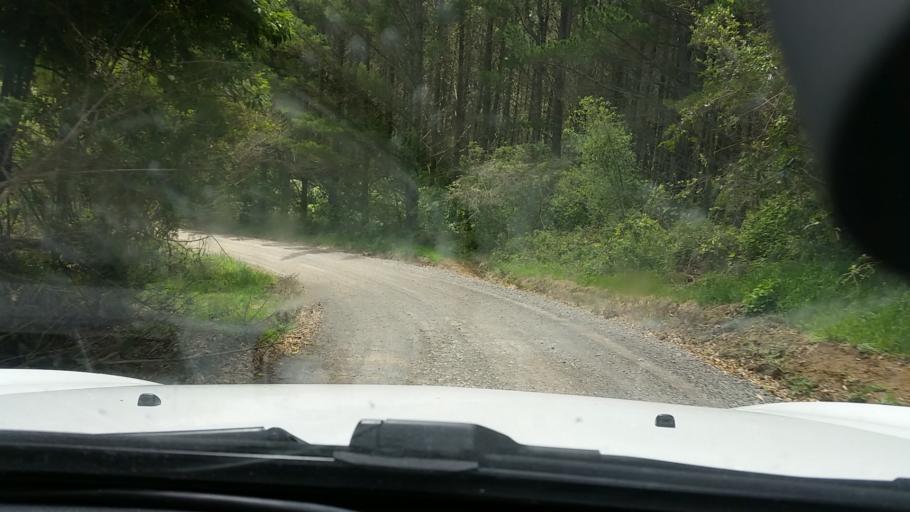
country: NZ
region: Bay of Plenty
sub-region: Kawerau District
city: Kawerau
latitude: -38.0047
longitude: 176.5540
